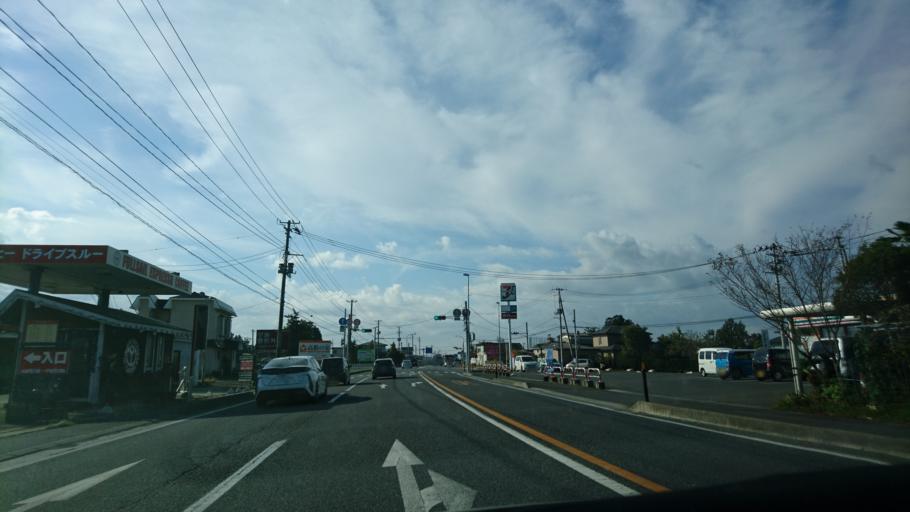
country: JP
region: Miyagi
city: Furukawa
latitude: 38.6081
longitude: 140.9825
